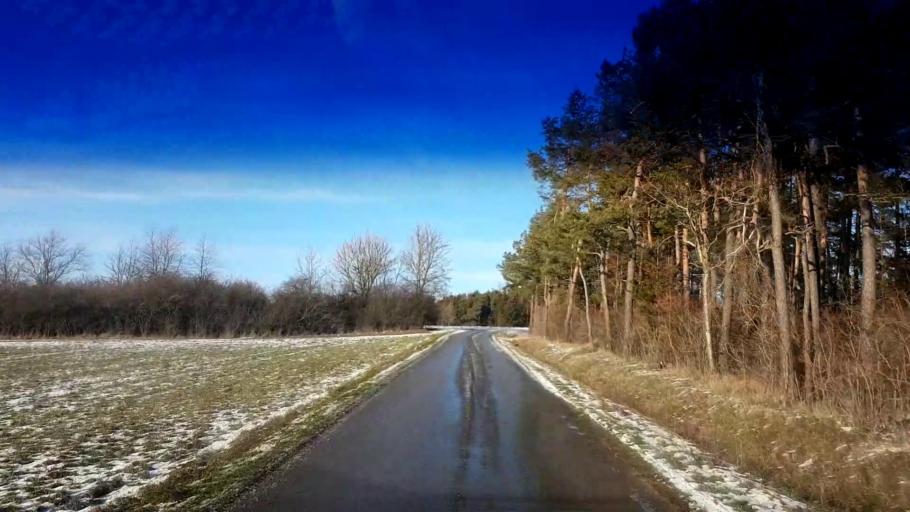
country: DE
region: Bavaria
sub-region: Upper Franconia
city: Heiligenstadt
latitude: 49.8420
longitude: 11.1038
